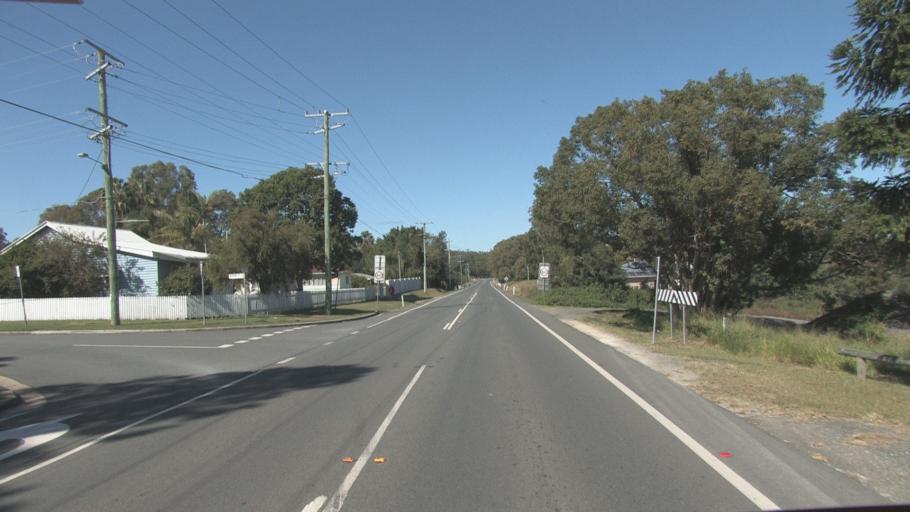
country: AU
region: Queensland
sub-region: Logan
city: Waterford West
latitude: -27.6966
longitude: 153.1445
